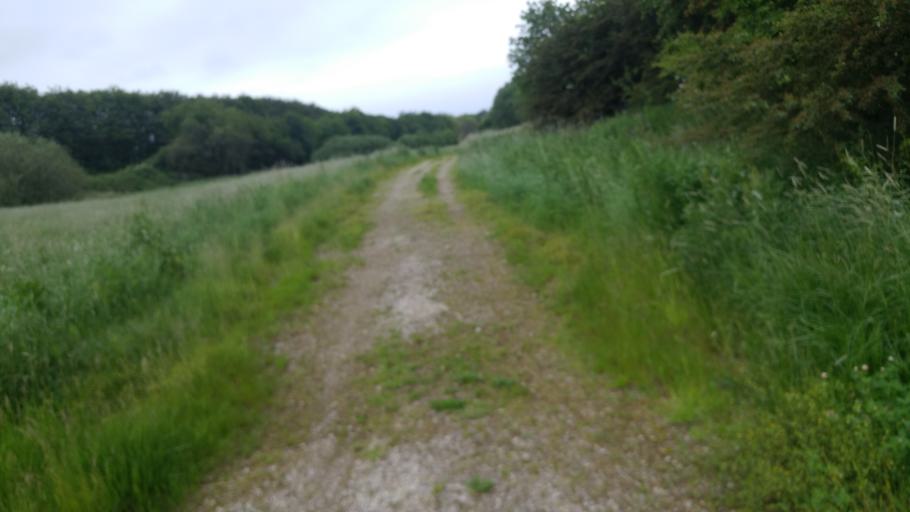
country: DK
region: Central Jutland
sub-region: Skanderborg Kommune
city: Horning
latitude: 56.0860
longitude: 10.0450
